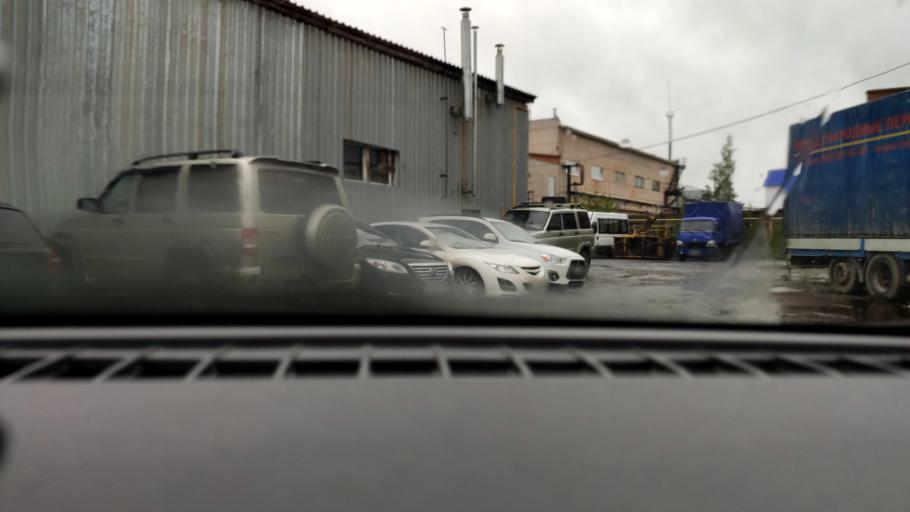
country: RU
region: Perm
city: Kondratovo
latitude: 57.9486
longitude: 56.1086
